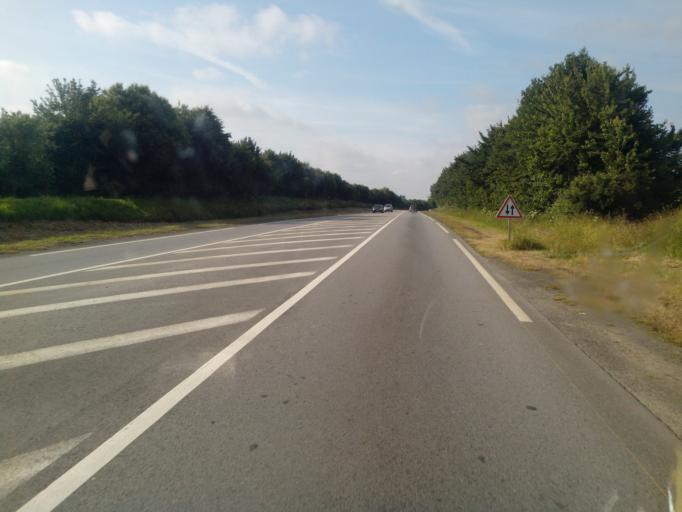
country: FR
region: Brittany
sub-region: Departement d'Ille-et-Vilaine
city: Chevaigne
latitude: 48.2366
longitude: -1.6218
